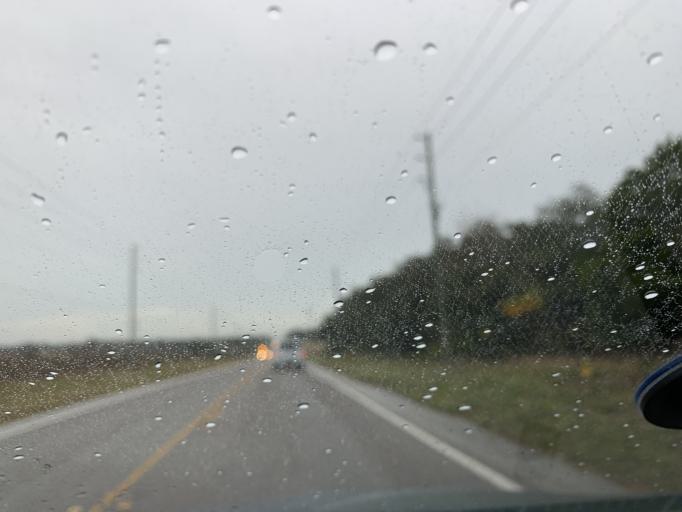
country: US
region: Florida
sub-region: Pasco County
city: Shady Hills
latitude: 28.4338
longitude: -82.5194
